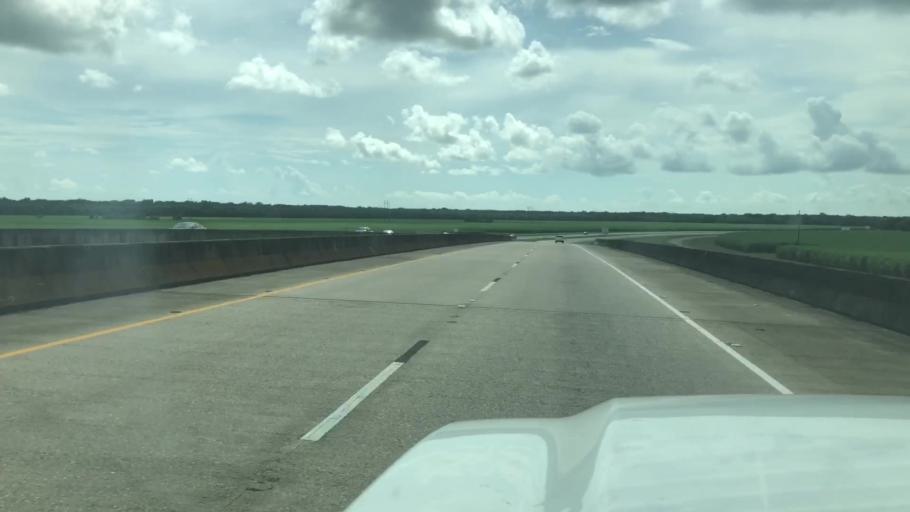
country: US
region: Louisiana
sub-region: Saint Mary Parish
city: Franklin
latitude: 29.7579
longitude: -91.4667
